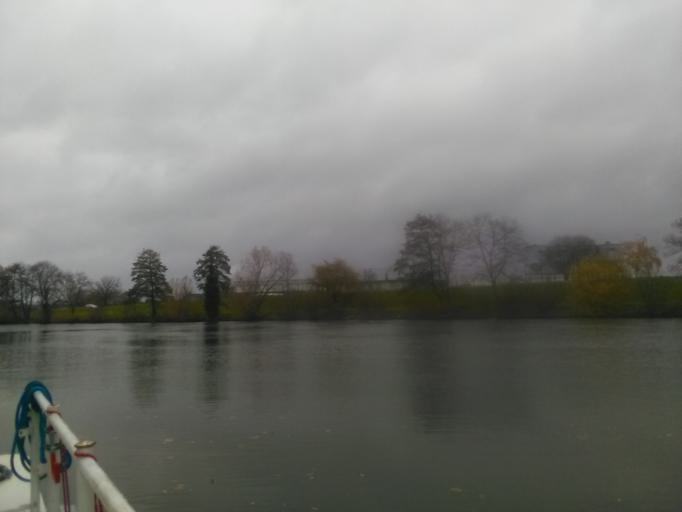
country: DE
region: Bavaria
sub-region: Upper Franconia
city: Hallstadt
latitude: 49.9068
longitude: 10.8601
